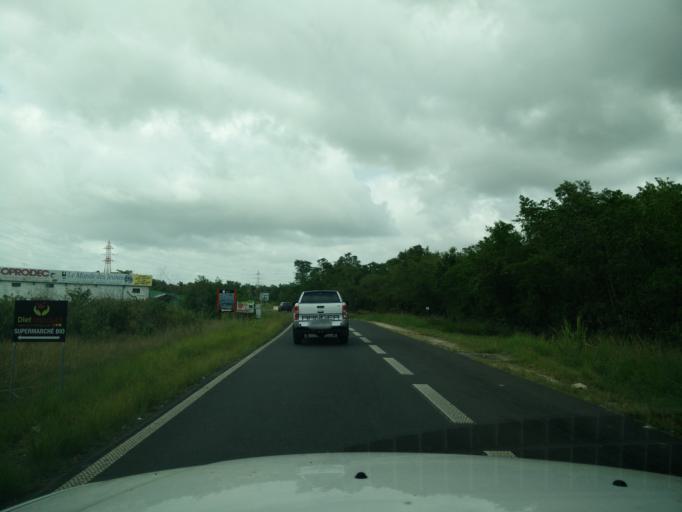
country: GP
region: Guadeloupe
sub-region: Guadeloupe
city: Pointe-a-Pitre
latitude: 16.2520
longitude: -61.5528
